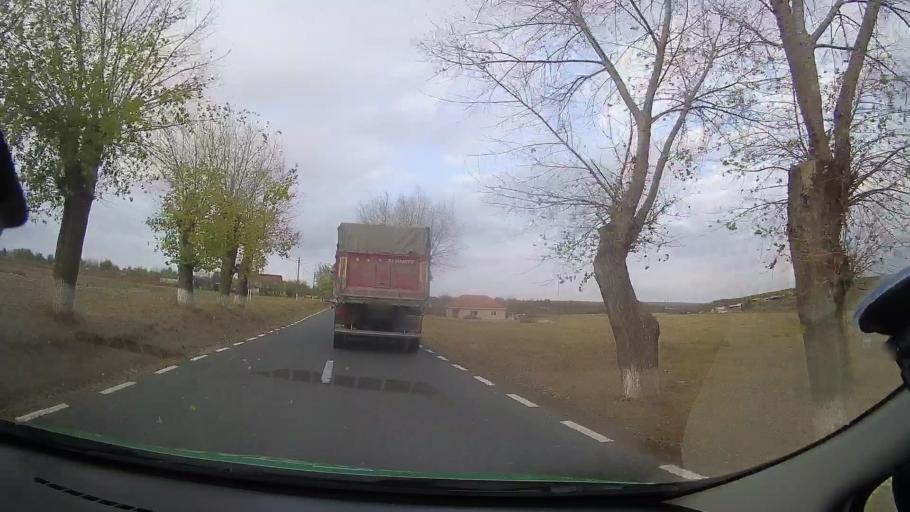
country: RO
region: Constanta
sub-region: Comuna Mircea Voda
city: Mircea Voda
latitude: 44.2732
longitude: 28.1720
